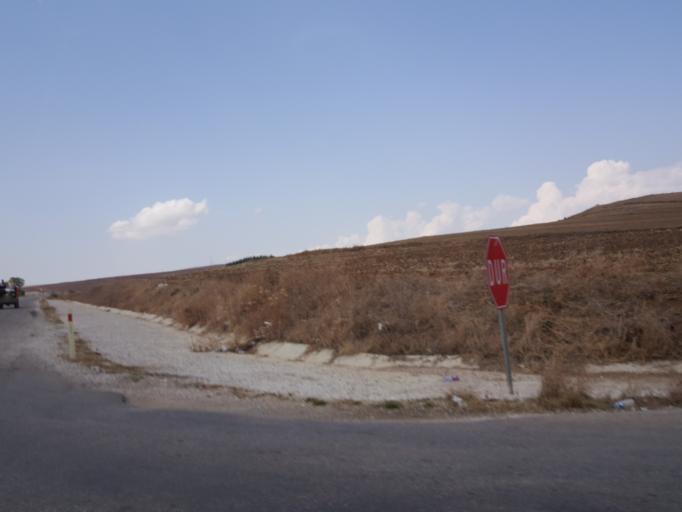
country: TR
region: Corum
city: Alaca
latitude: 40.1560
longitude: 34.7529
